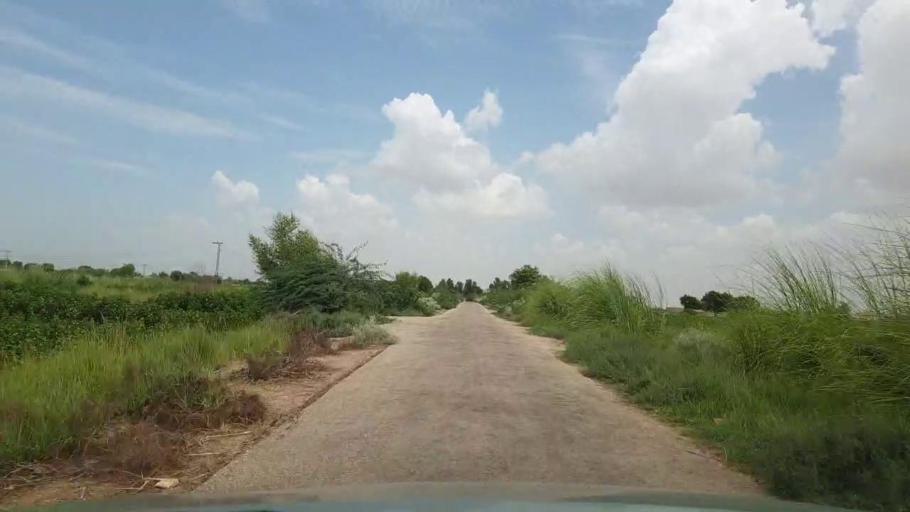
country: PK
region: Sindh
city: Bozdar
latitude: 27.0198
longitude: 68.9447
